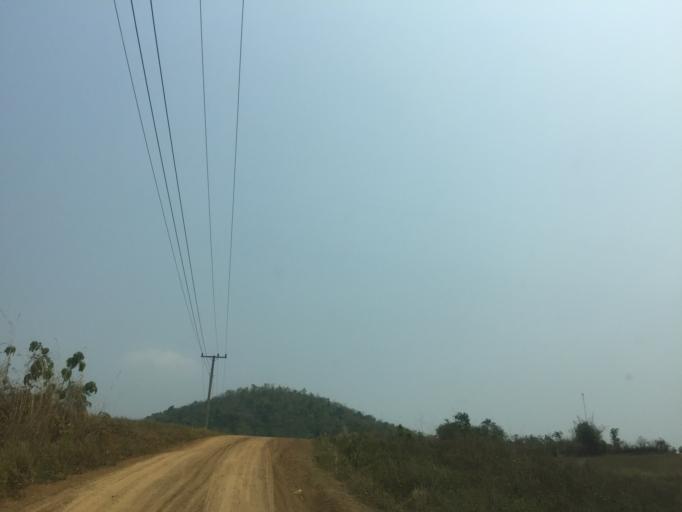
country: LA
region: Xiagnabouli
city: Muang Kenthao
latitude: 17.7948
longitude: 101.2573
